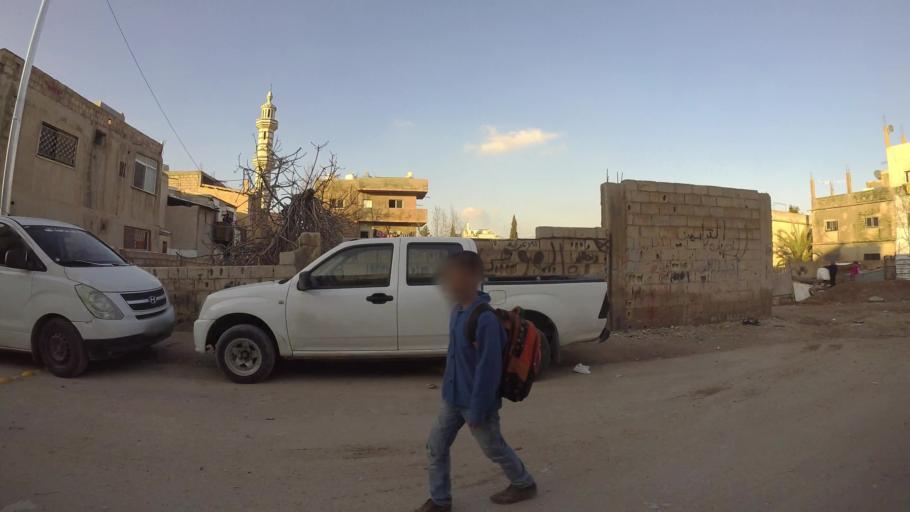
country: JO
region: Amman
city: Al Bunayyat ash Shamaliyah
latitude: 31.9086
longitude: 35.9152
